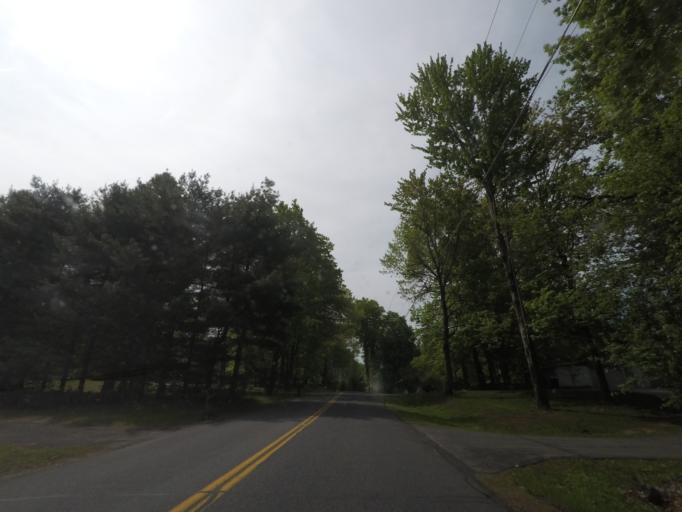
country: US
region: New York
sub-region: Saratoga County
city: Stillwater
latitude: 42.9777
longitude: -73.7152
